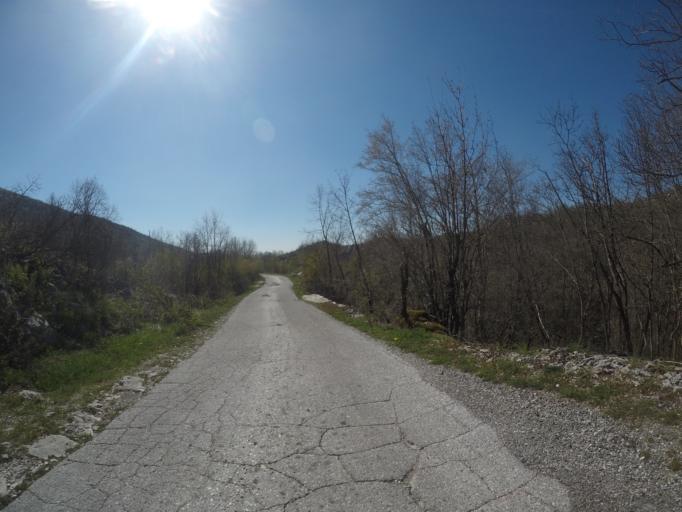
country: ME
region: Danilovgrad
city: Danilovgrad
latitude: 42.5399
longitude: 19.0102
